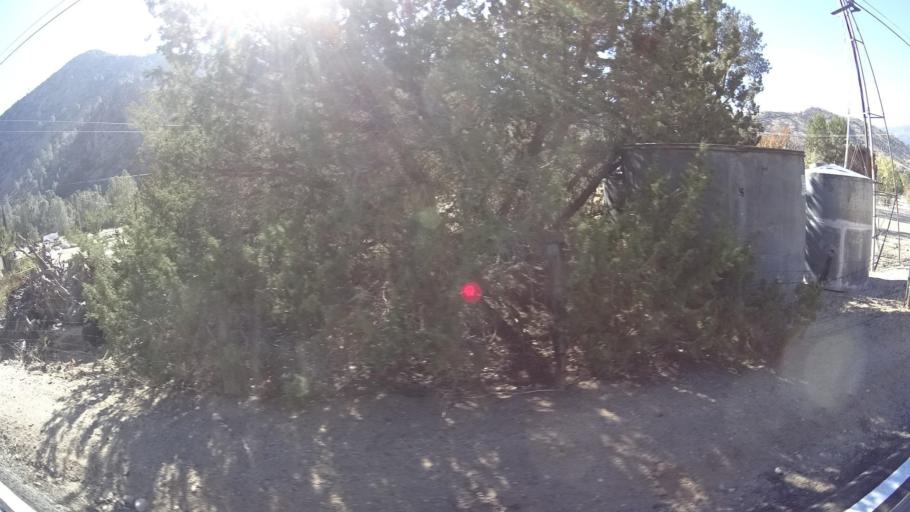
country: US
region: California
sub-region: Kern County
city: Lake Isabella
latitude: 35.5979
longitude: -118.4539
